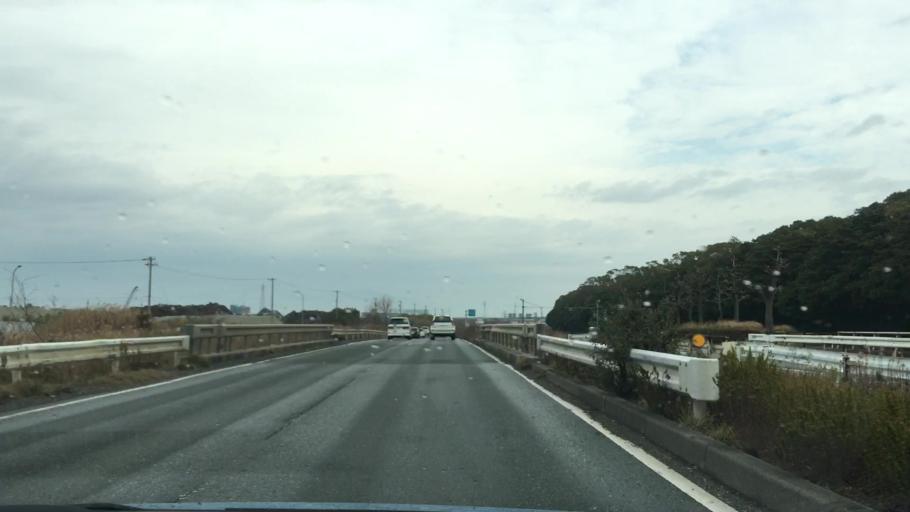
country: JP
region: Aichi
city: Toyohashi
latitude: 34.7206
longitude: 137.3412
